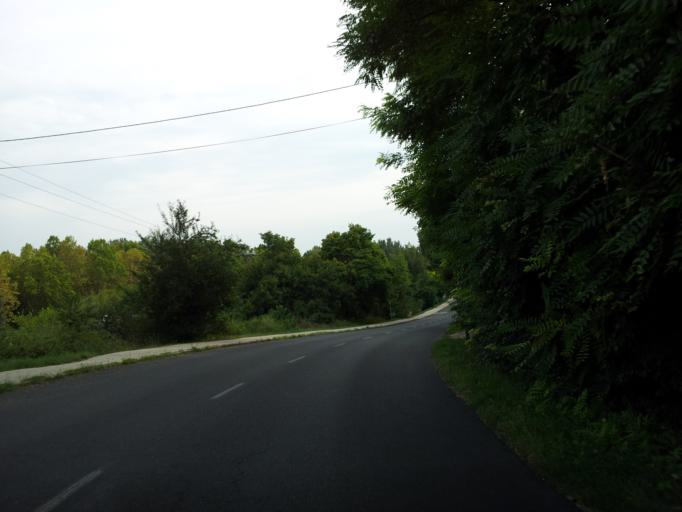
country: HU
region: Veszprem
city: Tihany
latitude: 46.8951
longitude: 17.8900
